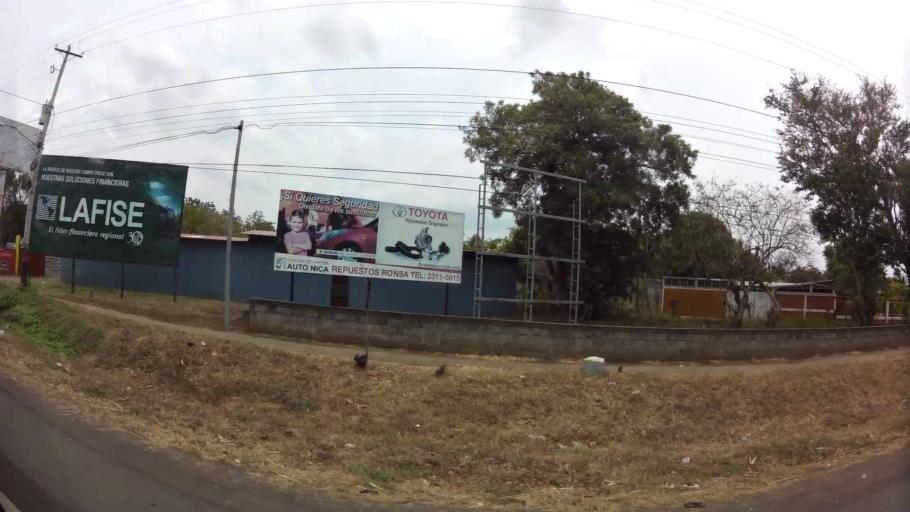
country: NI
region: Leon
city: Leon
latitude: 12.4178
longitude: -86.8691
